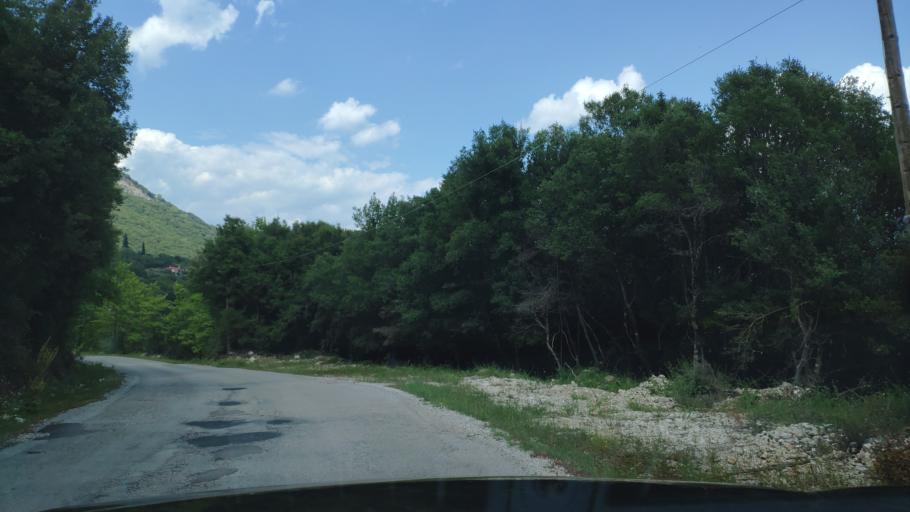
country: GR
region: Epirus
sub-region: Nomos Artas
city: Agios Dimitrios
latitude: 39.4392
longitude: 21.0147
